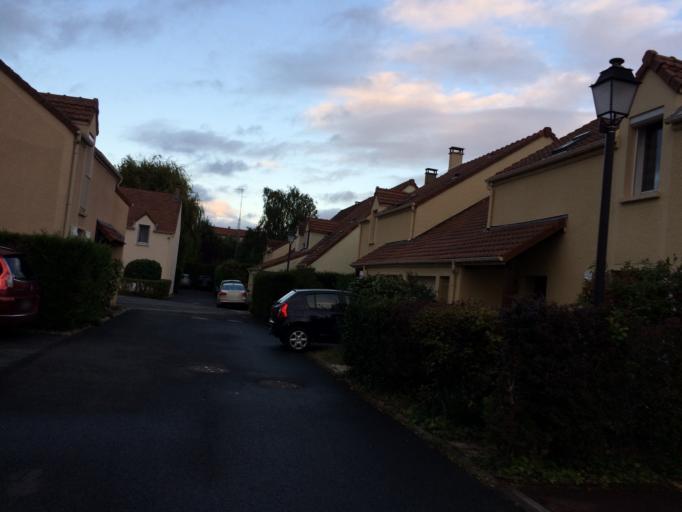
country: FR
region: Ile-de-France
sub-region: Departement des Hauts-de-Seine
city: Antony
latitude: 48.7383
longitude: 2.2949
